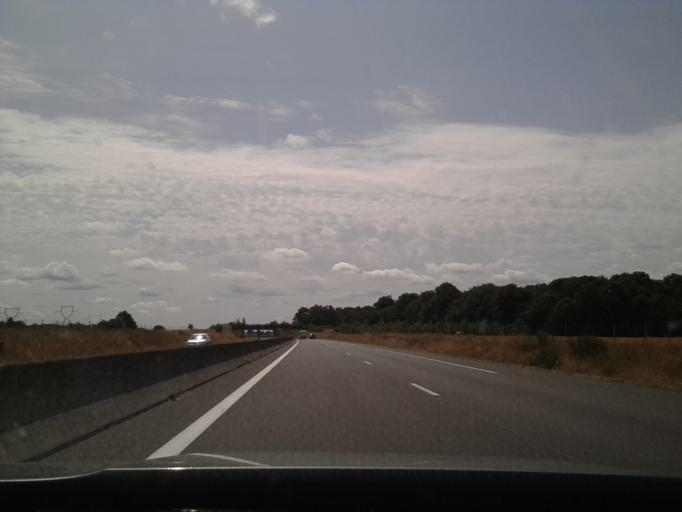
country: FR
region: Centre
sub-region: Departement d'Indre-et-Loire
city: Rouziers-de-Touraine
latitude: 47.5269
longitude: 0.6222
